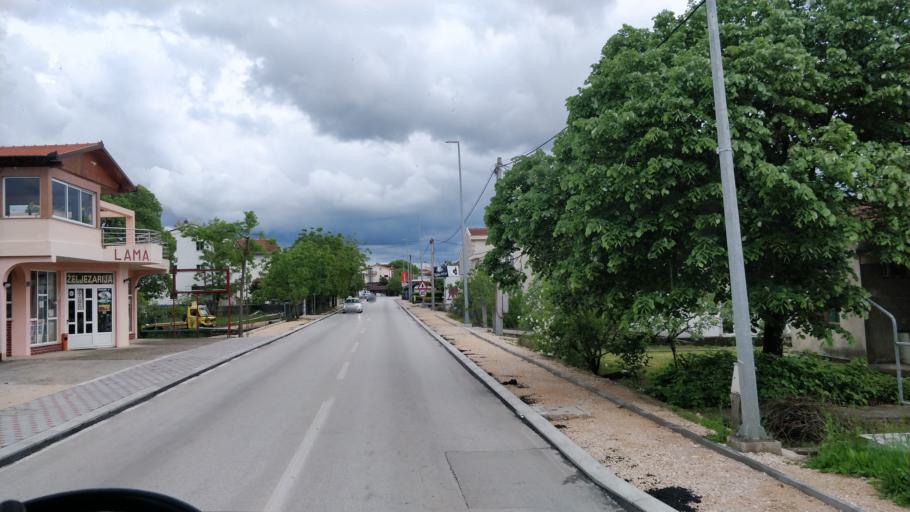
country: BA
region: Federation of Bosnia and Herzegovina
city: Ljubuski
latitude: 43.1903
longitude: 17.5352
